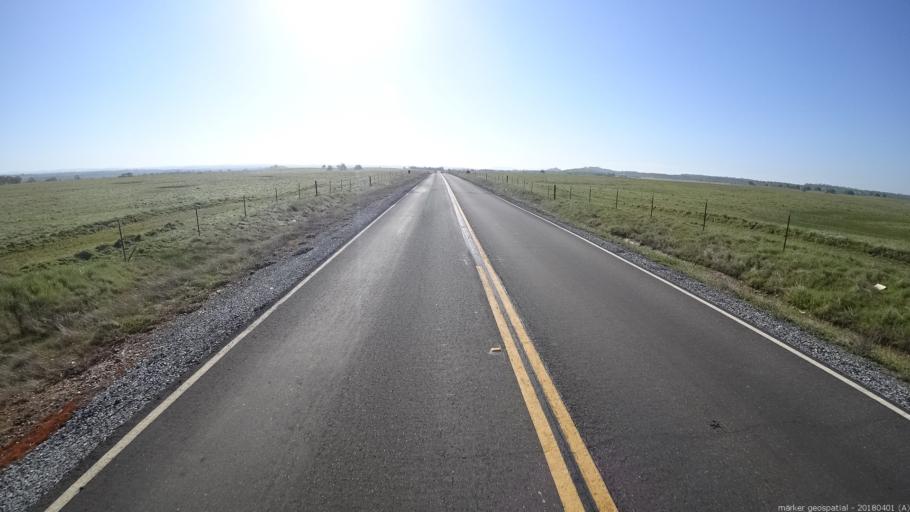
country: US
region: California
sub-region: Amador County
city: Ione
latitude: 38.4073
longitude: -121.0261
